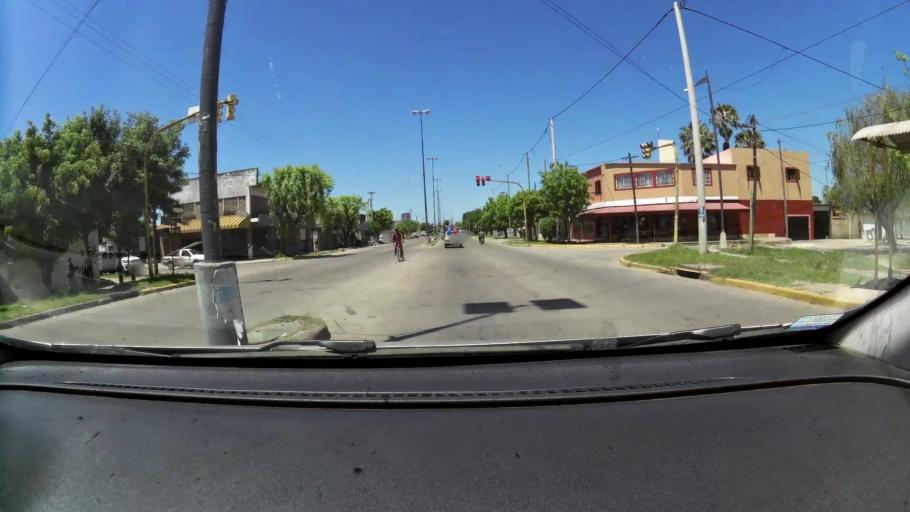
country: AR
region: Santa Fe
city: Santa Fe de la Vera Cruz
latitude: -31.6237
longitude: -60.7186
